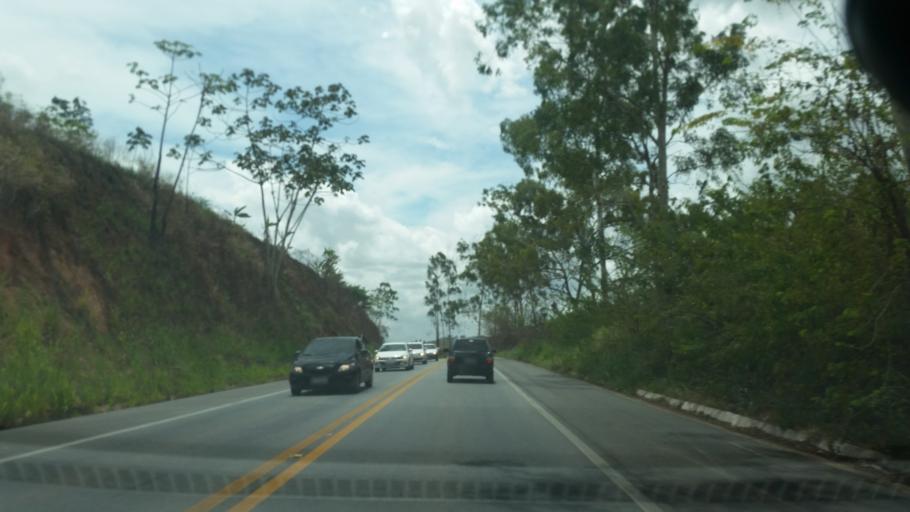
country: BR
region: Alagoas
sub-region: Uniao Dos Palmares
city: Uniao dos Palmares
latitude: -9.2073
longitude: -36.0323
